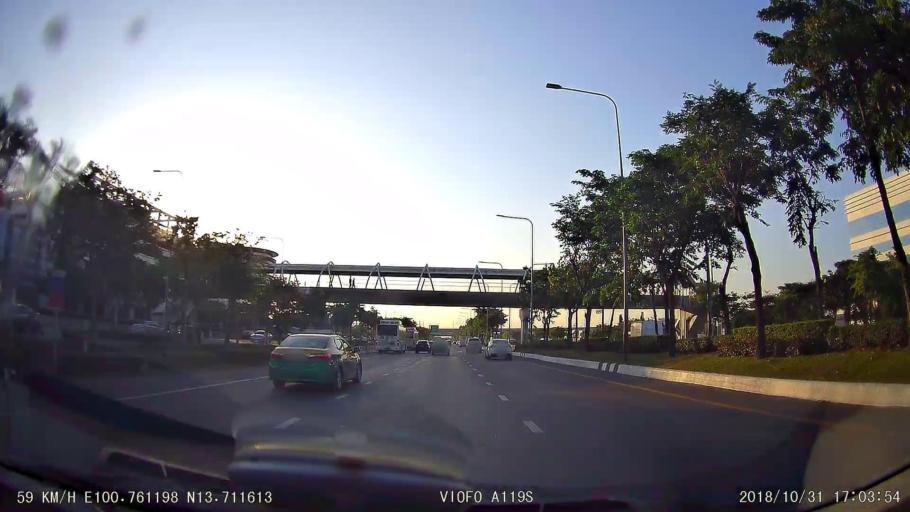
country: TH
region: Bangkok
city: Lat Krabang
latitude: 13.7116
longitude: 100.7612
